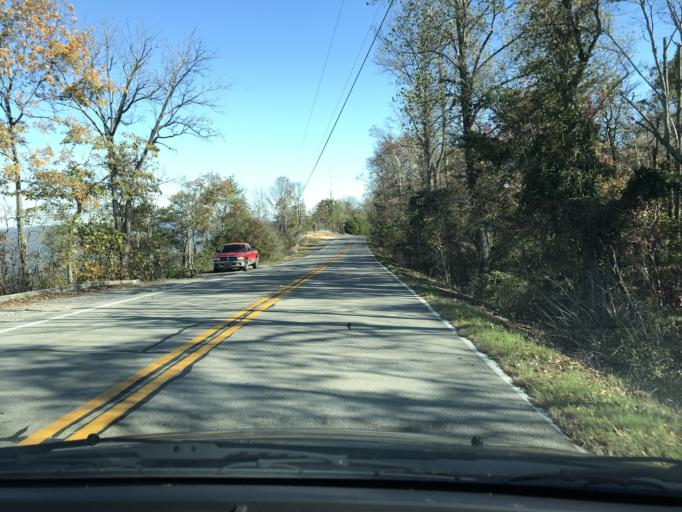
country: US
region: Georgia
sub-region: Dade County
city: Trenton
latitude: 34.8966
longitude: -85.4457
